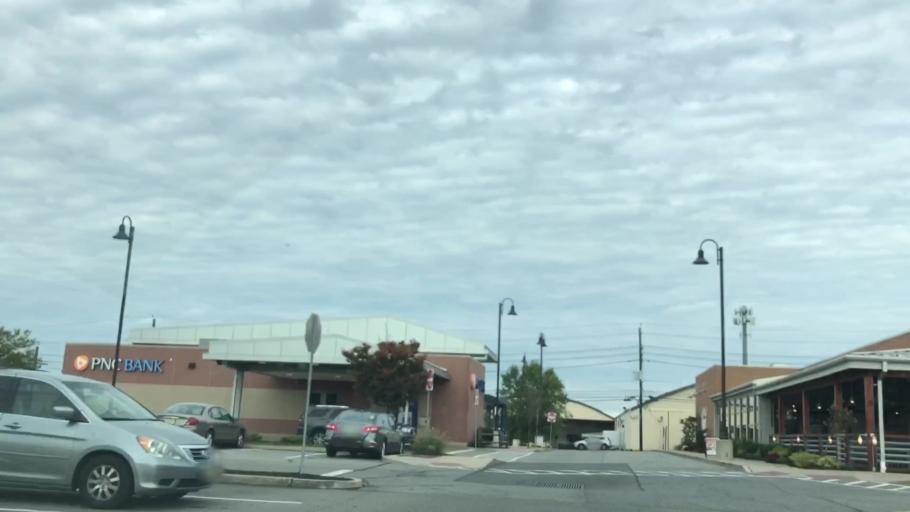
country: US
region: New Jersey
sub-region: Essex County
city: Nutley
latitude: 40.8398
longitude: -74.1566
